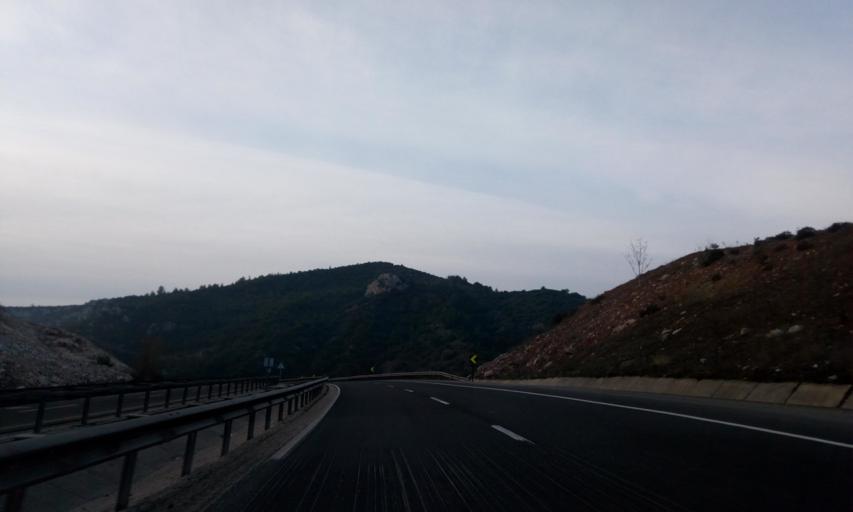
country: TR
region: Bilecik
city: Bilecik
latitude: 40.1589
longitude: 30.0187
